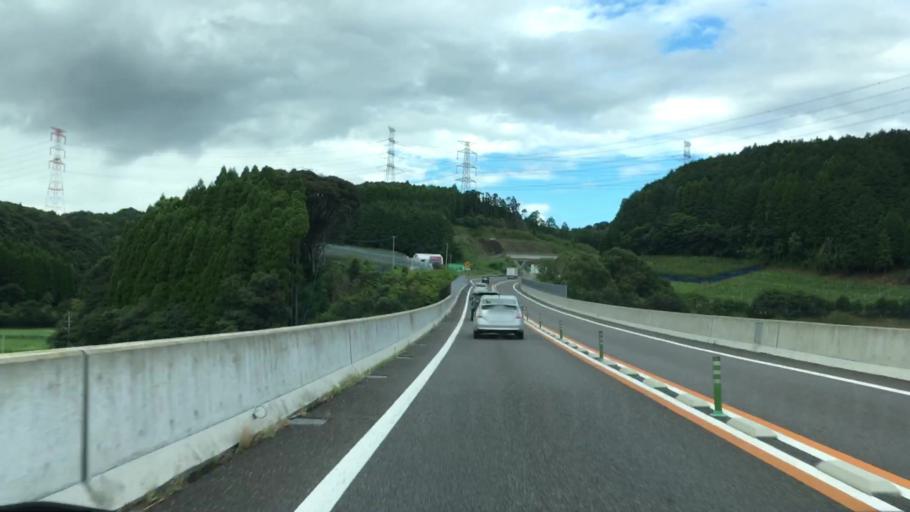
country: JP
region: Saga Prefecture
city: Imaricho-ko
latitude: 33.3483
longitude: 129.9246
